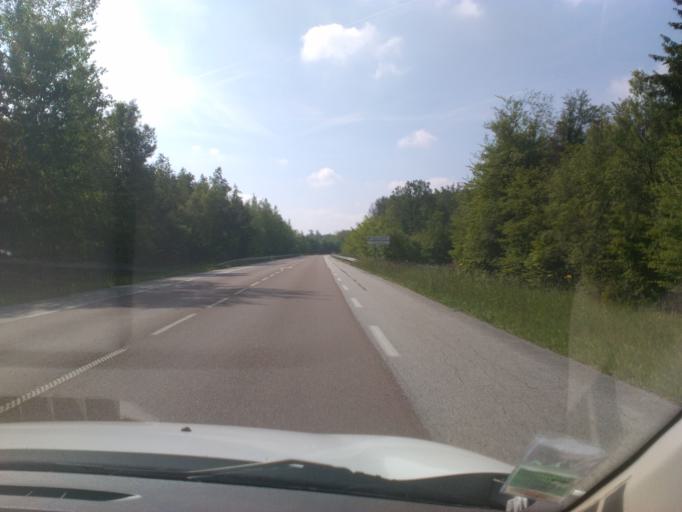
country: FR
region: Lorraine
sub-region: Departement des Vosges
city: Les Forges
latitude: 48.1985
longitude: 6.3961
